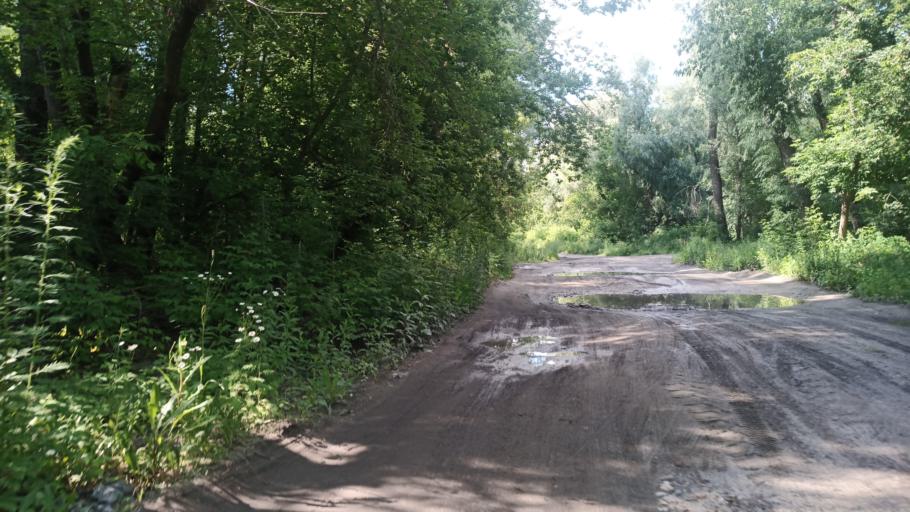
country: RU
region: Altai Krai
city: Zaton
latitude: 53.3368
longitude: 83.8070
